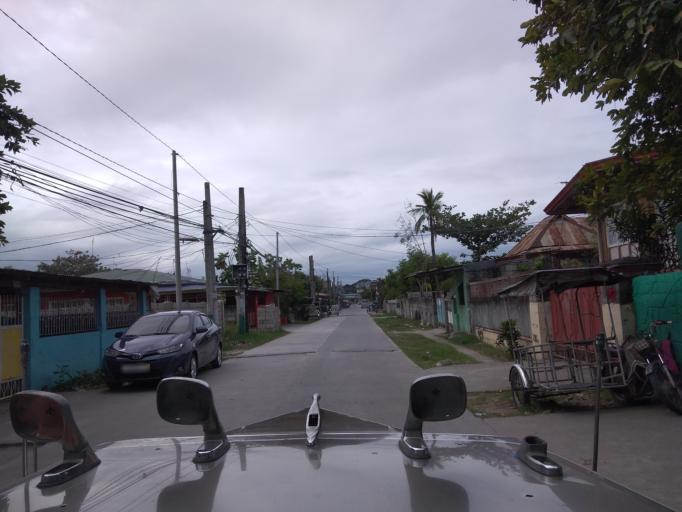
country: PH
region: Central Luzon
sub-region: Province of Pampanga
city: Mexico
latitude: 15.0648
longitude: 120.7181
